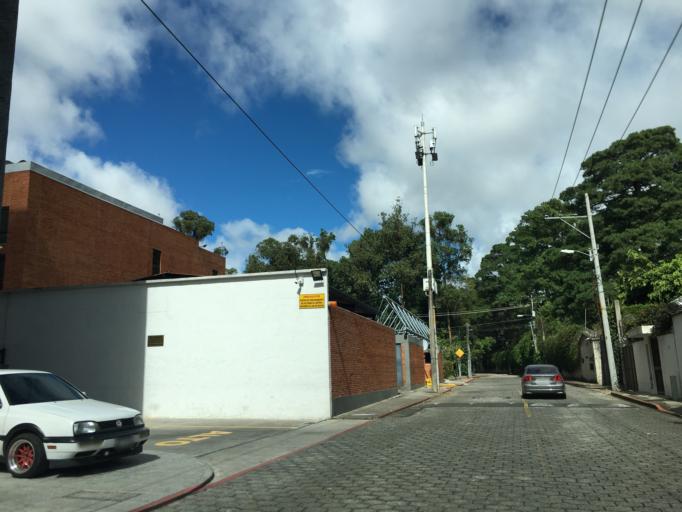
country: GT
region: Guatemala
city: Santa Catarina Pinula
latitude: 14.5893
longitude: -90.5186
